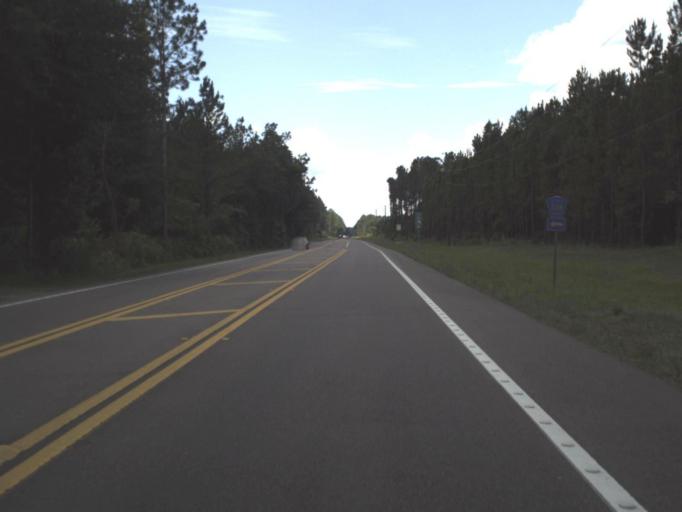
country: US
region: Florida
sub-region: Alachua County
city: Waldo
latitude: 29.7011
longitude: -82.1786
